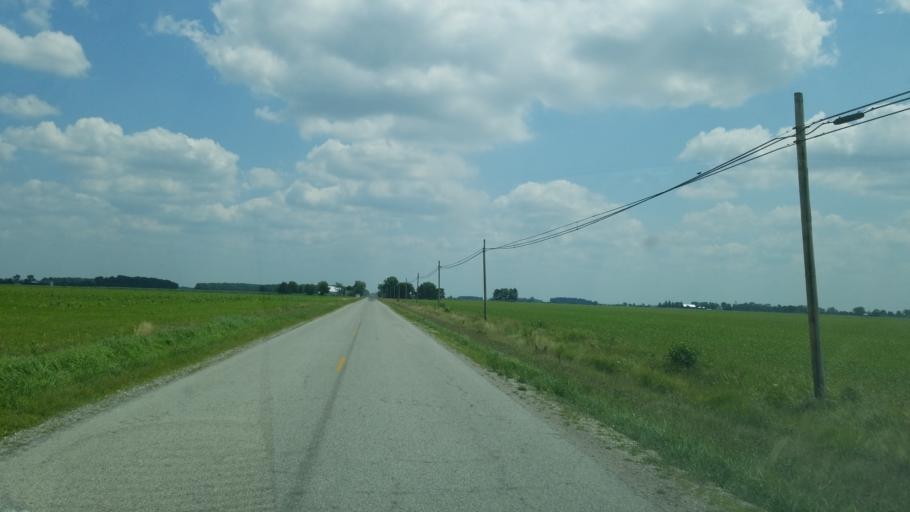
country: US
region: Ohio
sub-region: Henry County
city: Napoleon
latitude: 41.3416
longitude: -84.0550
